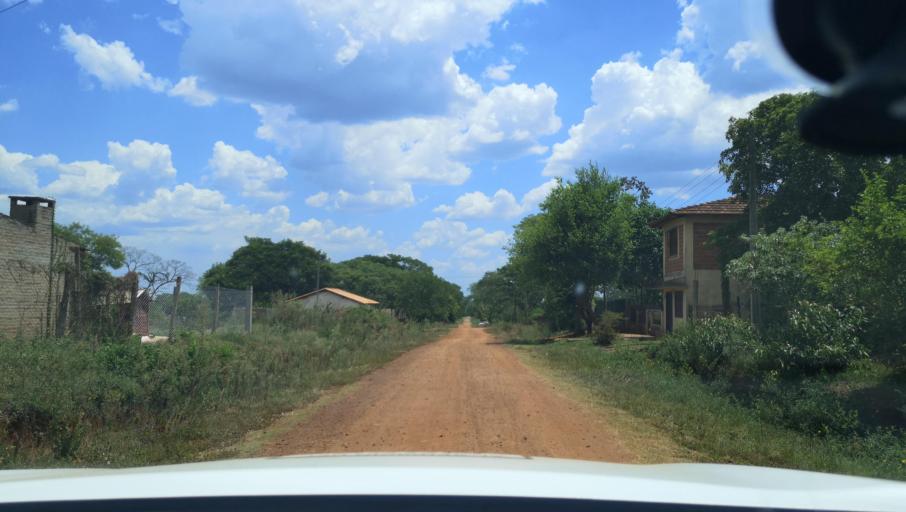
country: PY
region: Itapua
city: Carmen del Parana
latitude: -27.1676
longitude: -56.2372
